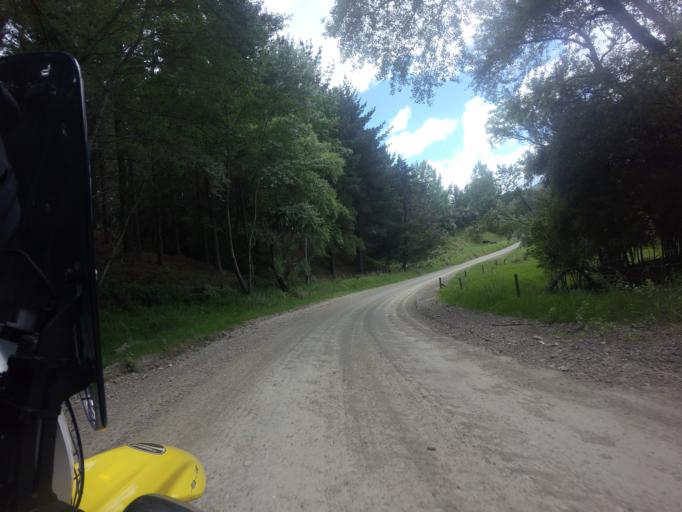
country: NZ
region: Hawke's Bay
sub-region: Wairoa District
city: Wairoa
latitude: -39.0048
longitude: 177.7605
